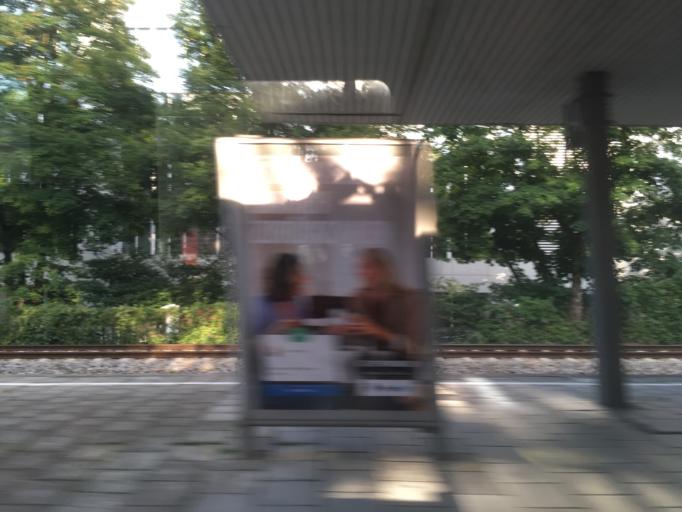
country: DE
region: Bavaria
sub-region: Upper Bavaria
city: Munich
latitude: 48.1190
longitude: 11.5959
